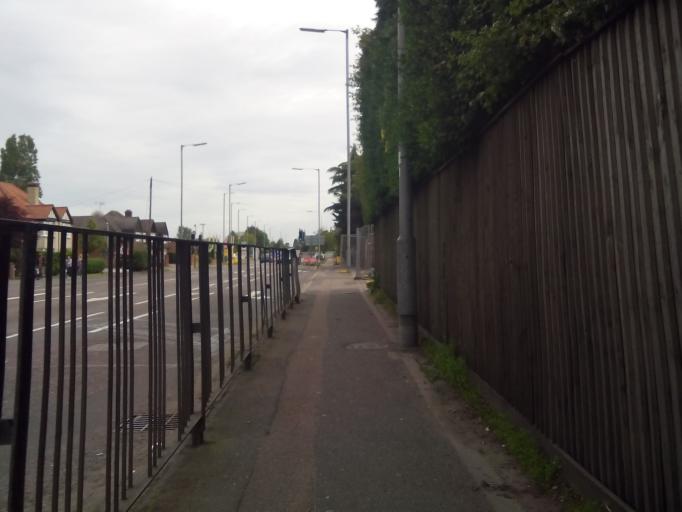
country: GB
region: England
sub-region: Cambridgeshire
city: Cambridge
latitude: 52.2274
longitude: 0.1459
